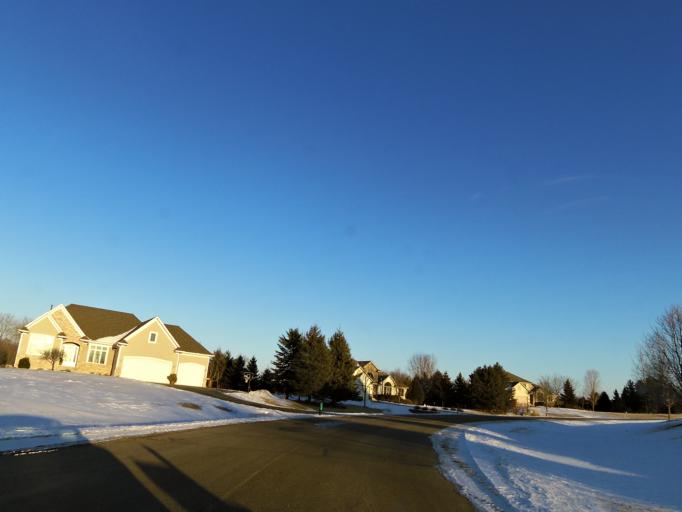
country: US
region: Minnesota
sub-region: Washington County
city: Lake Elmo
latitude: 44.9883
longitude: -92.8572
